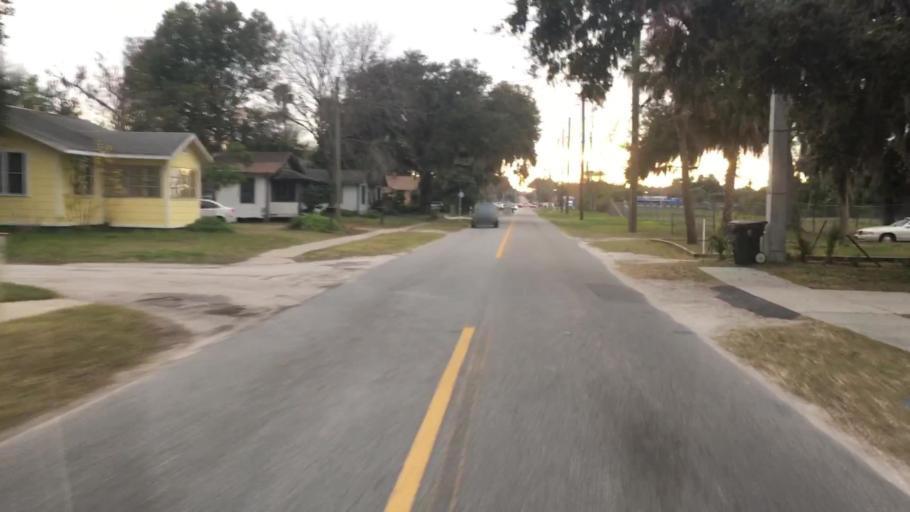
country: US
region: Florida
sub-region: Volusia County
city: Daytona Beach
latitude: 29.2180
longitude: -81.0431
